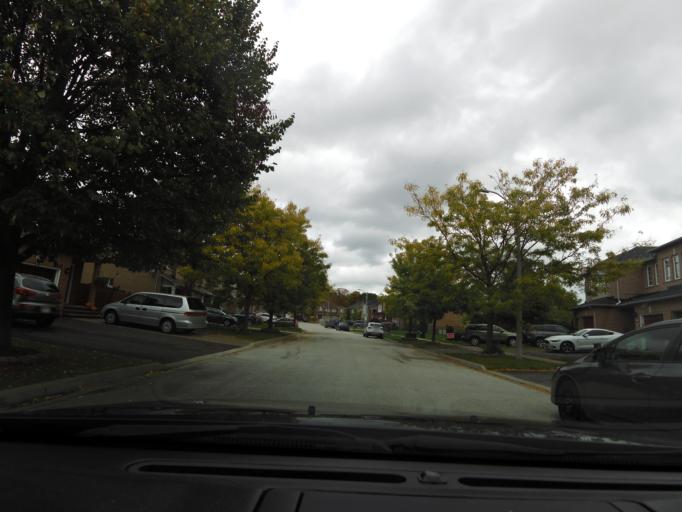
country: CA
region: Ontario
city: Burlington
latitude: 43.3926
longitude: -79.7789
